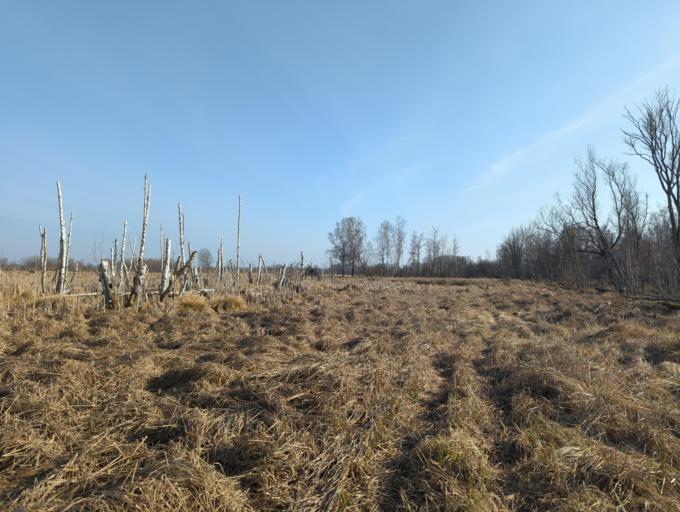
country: DE
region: Bavaria
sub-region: Swabia
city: Leipheim
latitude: 48.4823
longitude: 10.2032
